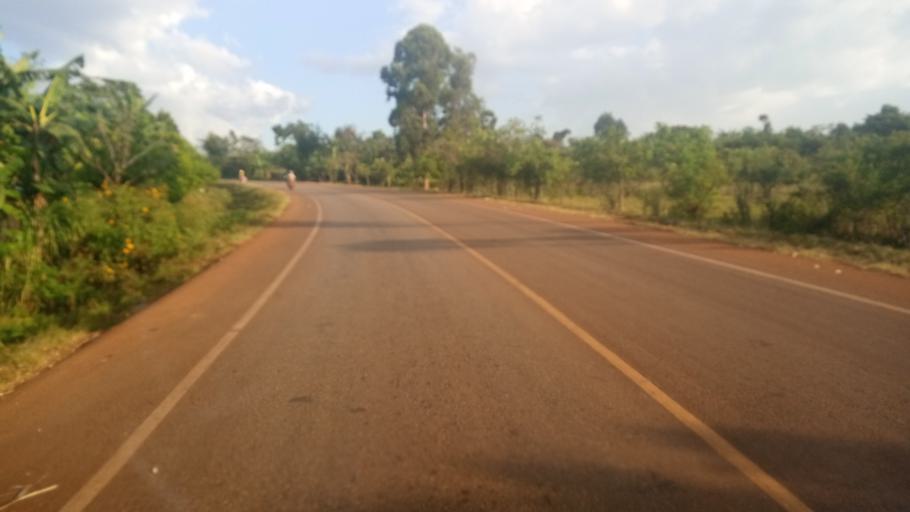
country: UG
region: Eastern Region
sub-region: Sironko District
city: Sironko
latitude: 1.3246
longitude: 34.3305
